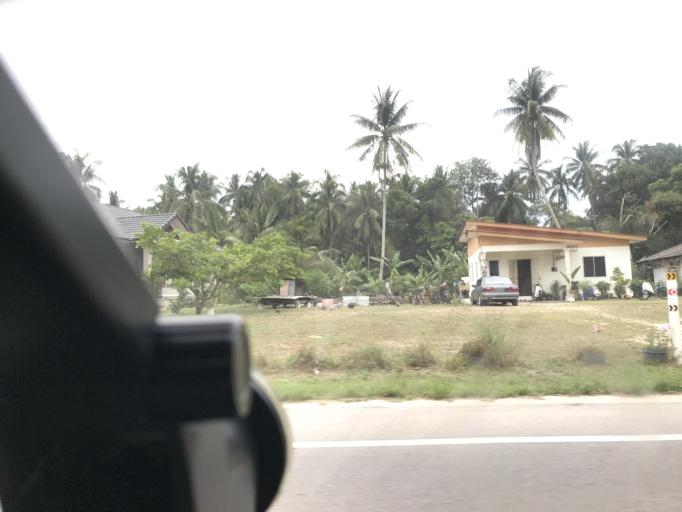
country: MY
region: Kelantan
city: Tumpat
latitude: 6.1742
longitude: 102.2085
